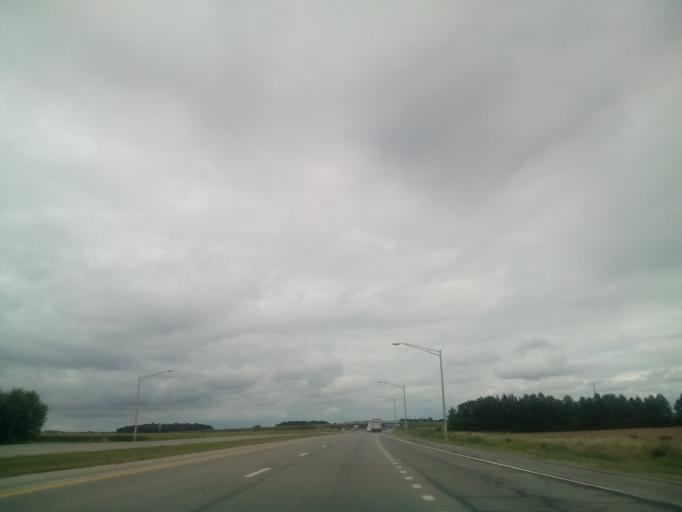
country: US
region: Ohio
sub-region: Fulton County
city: Burlington
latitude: 41.5917
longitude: -84.3148
